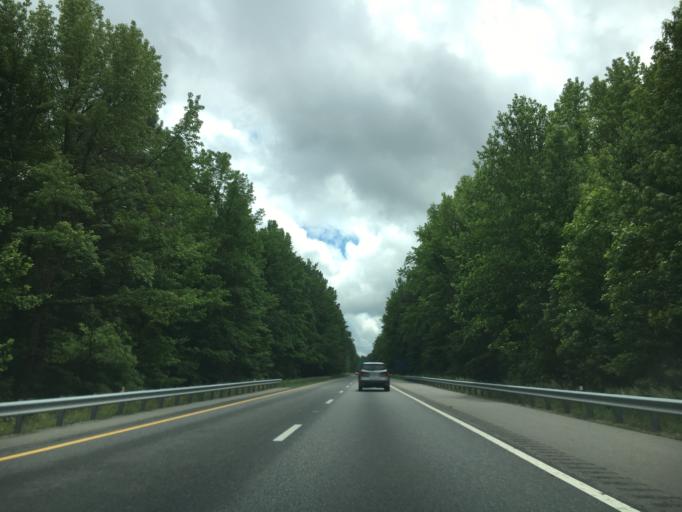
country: US
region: Virginia
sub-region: Mecklenburg County
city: South Hill
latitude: 36.7297
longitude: -78.1055
